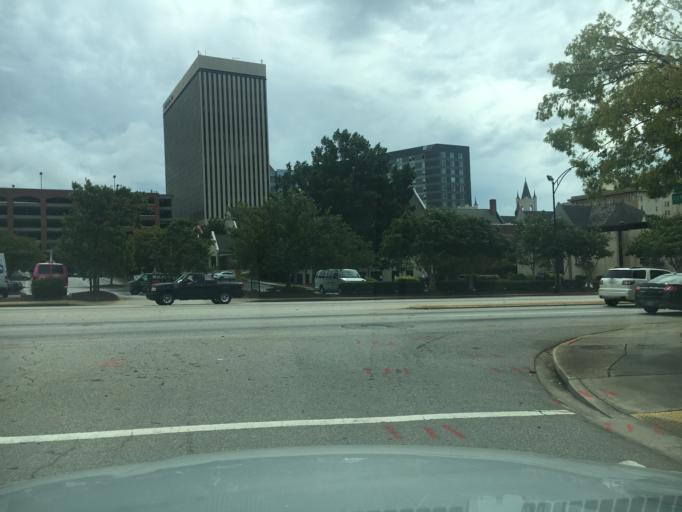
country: US
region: South Carolina
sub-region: Greenville County
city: Greenville
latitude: 34.8532
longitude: -82.4017
